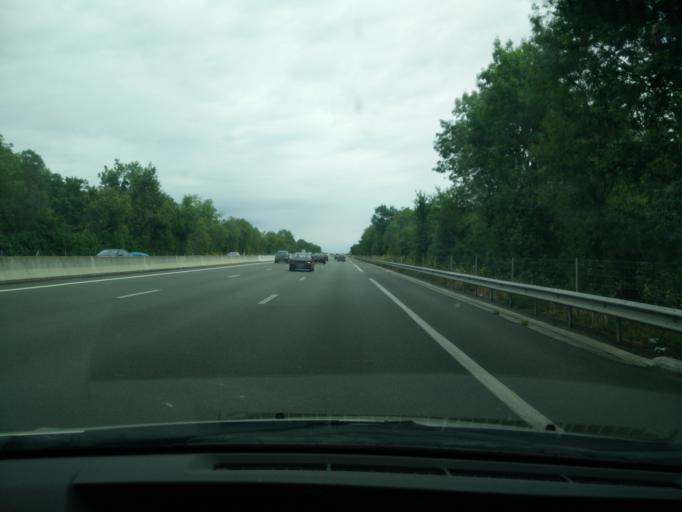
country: FR
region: Pays de la Loire
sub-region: Departement de Maine-et-Loire
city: Les Ponts-de-Ce
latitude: 47.4064
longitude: -0.5093
